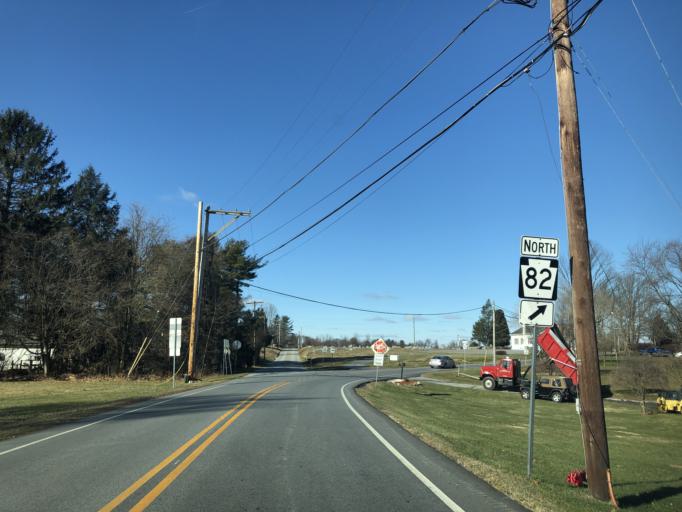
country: US
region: Pennsylvania
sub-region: Chester County
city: South Coatesville
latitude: 39.9469
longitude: -75.8400
